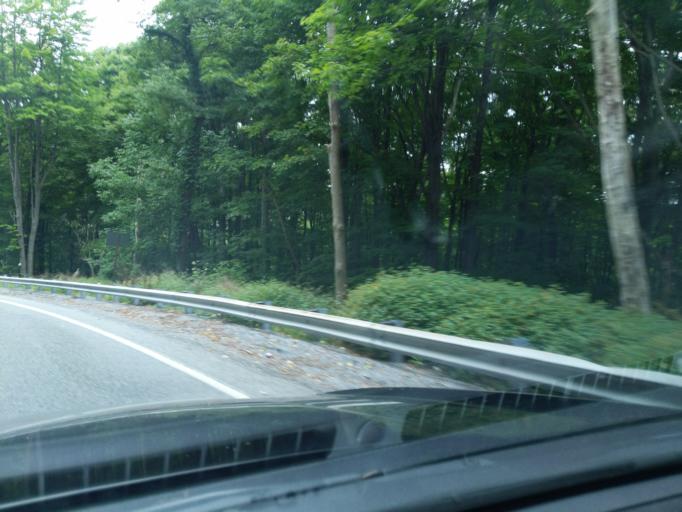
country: US
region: Pennsylvania
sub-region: Cambria County
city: Cresson
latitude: 40.3581
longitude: -78.5509
